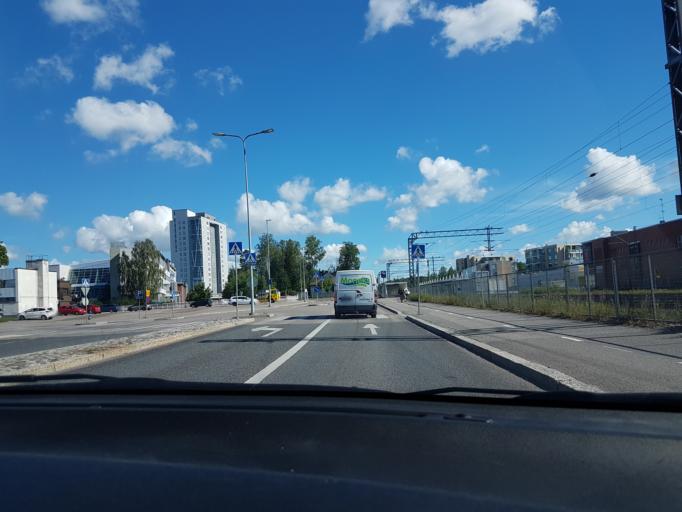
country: FI
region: Uusimaa
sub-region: Helsinki
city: Kerava
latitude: 60.3496
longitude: 25.0773
